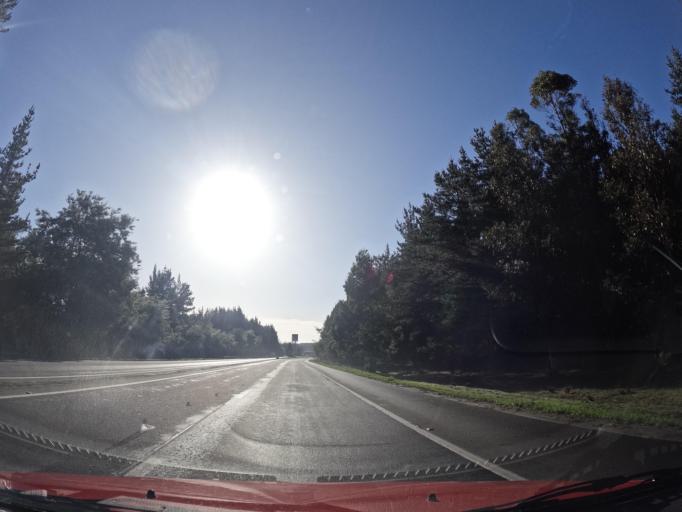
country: CL
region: Biobio
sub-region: Provincia de Concepcion
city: Penco
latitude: -36.7507
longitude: -72.9229
